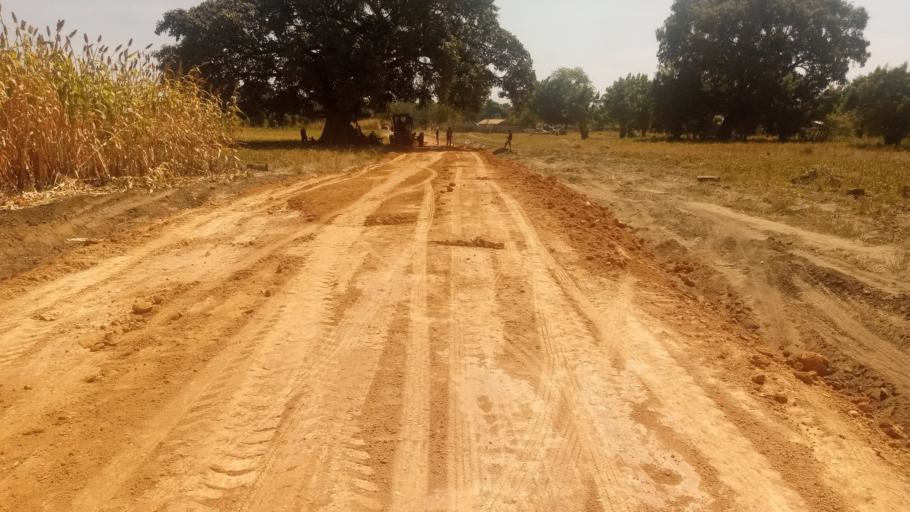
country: NG
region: Adamawa
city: Madagali
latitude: 10.8391
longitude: 13.3988
